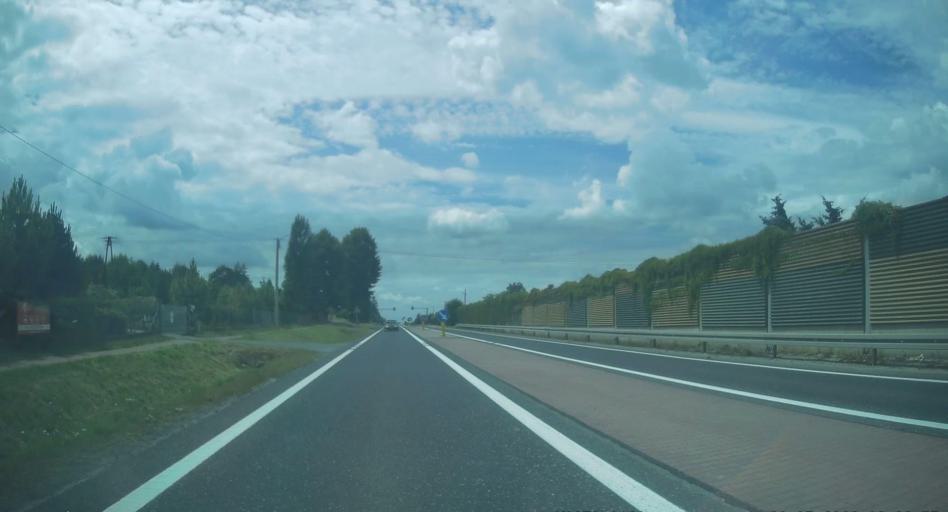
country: PL
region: Subcarpathian Voivodeship
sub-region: Powiat ropczycko-sedziszowski
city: Ostrow
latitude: 50.0620
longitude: 21.5488
